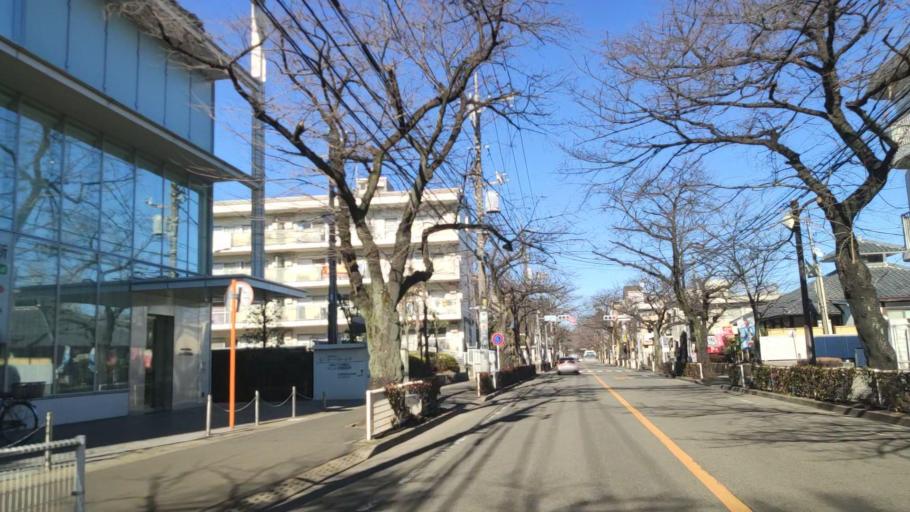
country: JP
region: Tokyo
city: Musashino
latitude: 35.7152
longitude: 139.5652
